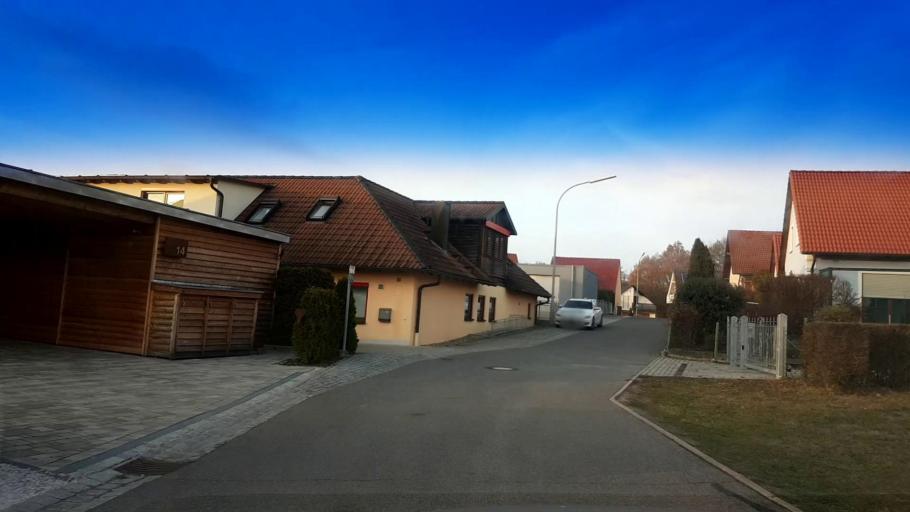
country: DE
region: Bavaria
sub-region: Upper Franconia
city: Schesslitz
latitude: 49.9735
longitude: 10.9876
